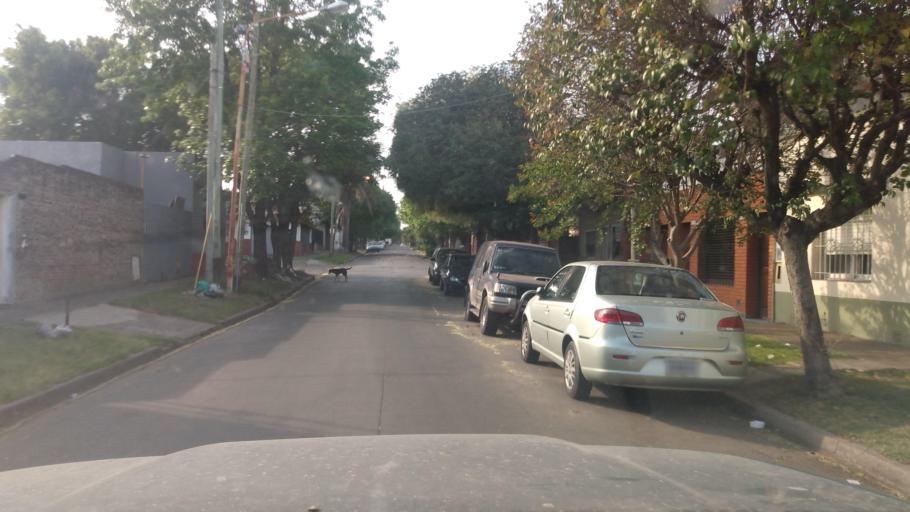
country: AR
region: Buenos Aires
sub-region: Partido de Moron
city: Moron
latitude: -34.6361
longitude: -58.6199
